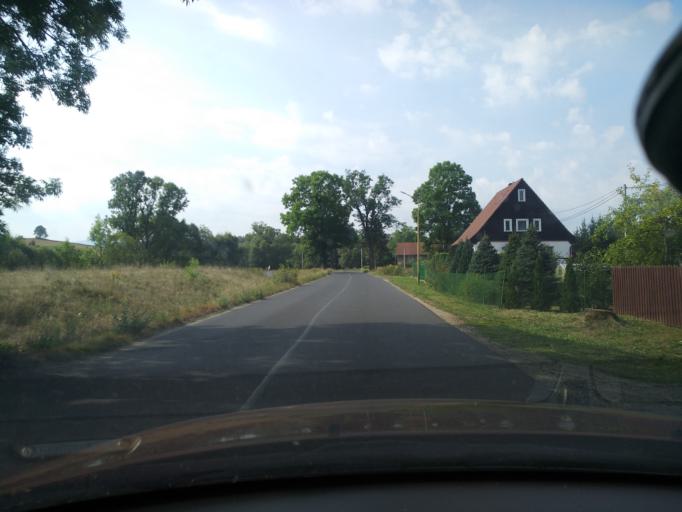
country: PL
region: Lower Silesian Voivodeship
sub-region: Powiat jeleniogorski
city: Stara Kamienica
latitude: 50.9320
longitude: 15.5822
